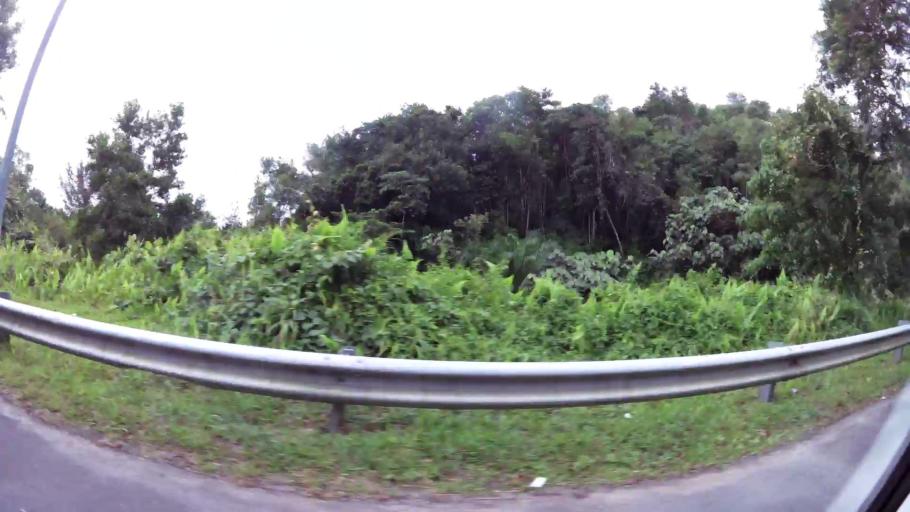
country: BN
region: Brunei and Muara
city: Bandar Seri Begawan
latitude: 4.8768
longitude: 114.8979
